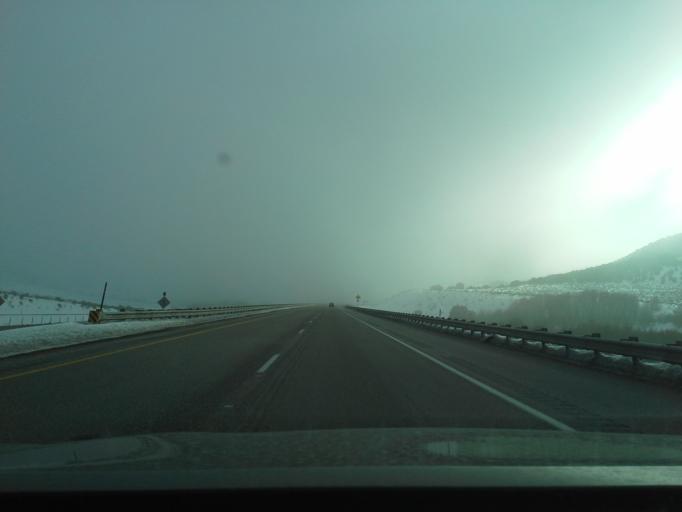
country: US
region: Idaho
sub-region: Oneida County
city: Malad City
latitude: 42.3718
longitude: -112.2116
